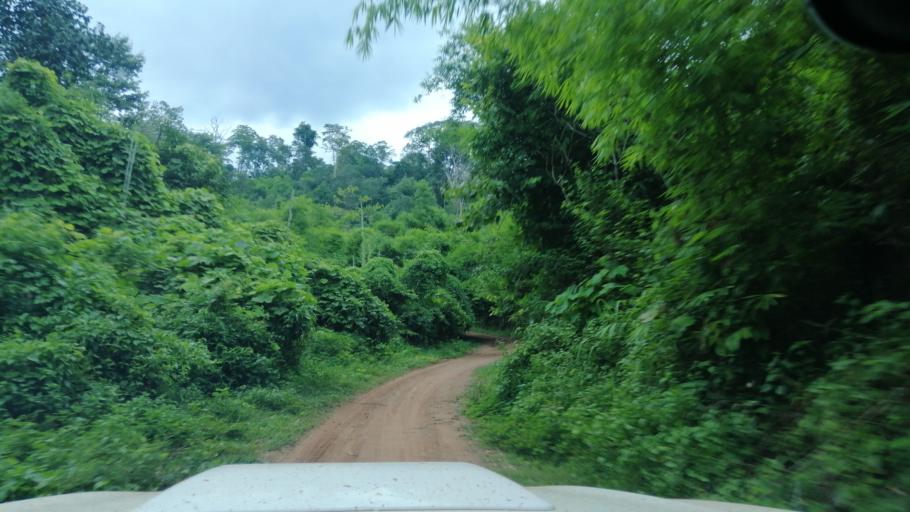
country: TH
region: Nan
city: Mae Charim
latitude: 18.7663
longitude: 101.3079
